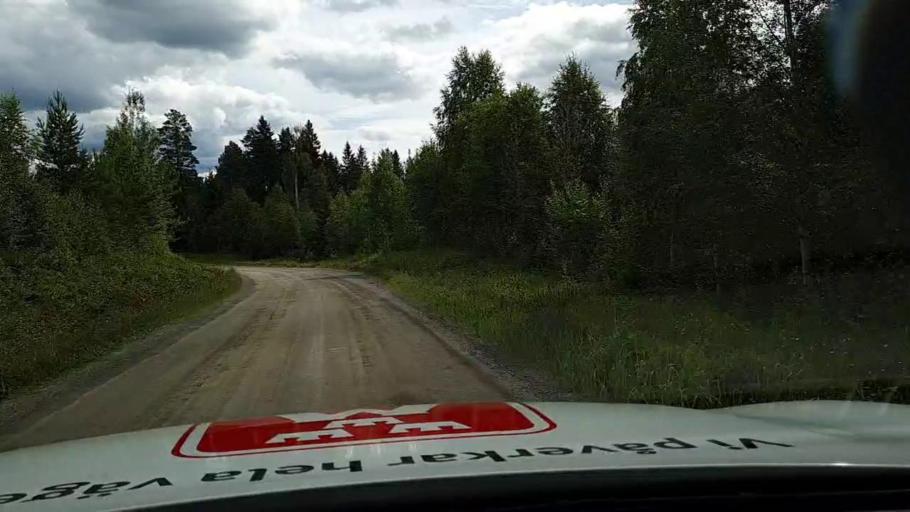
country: SE
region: Jaemtland
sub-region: Braecke Kommun
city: Braecke
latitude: 63.2209
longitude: 15.3463
